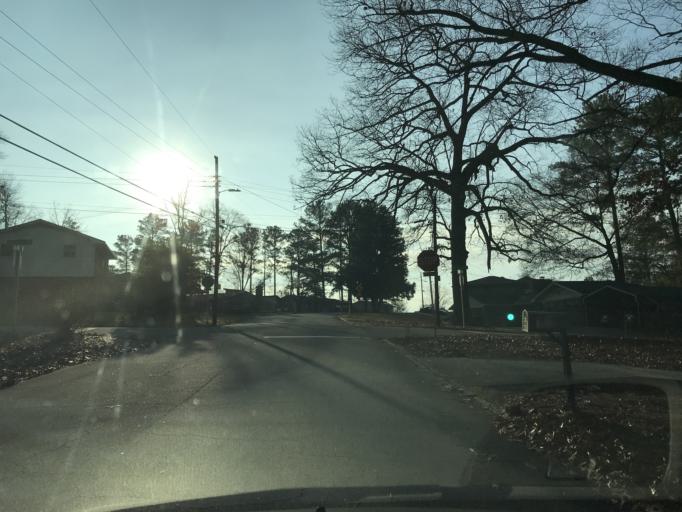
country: US
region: Georgia
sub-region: Clayton County
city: Riverdale
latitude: 33.6130
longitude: -84.4299
